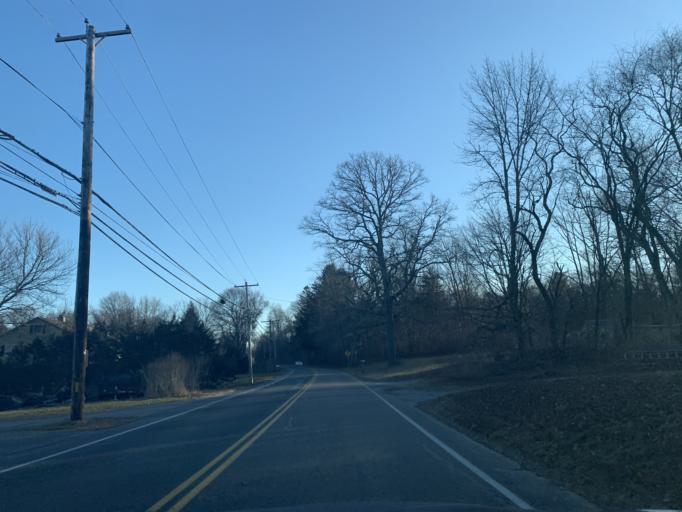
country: US
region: Massachusetts
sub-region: Bristol County
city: Rehoboth
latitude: 41.8802
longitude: -71.2302
